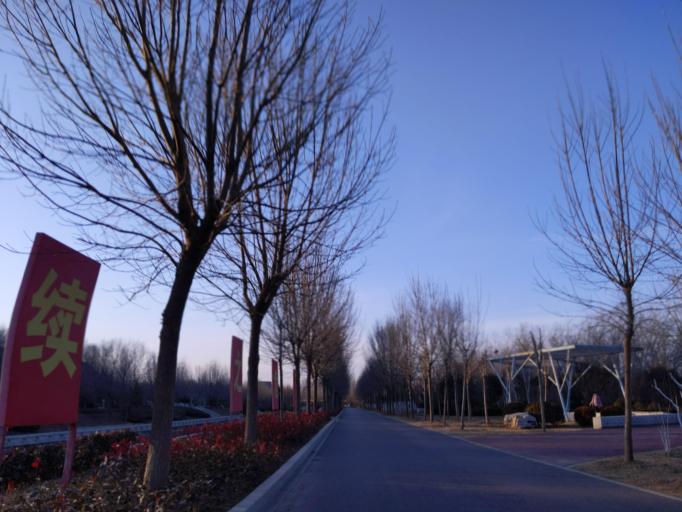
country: CN
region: Henan Sheng
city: Puyang
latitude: 35.7676
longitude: 115.0002
